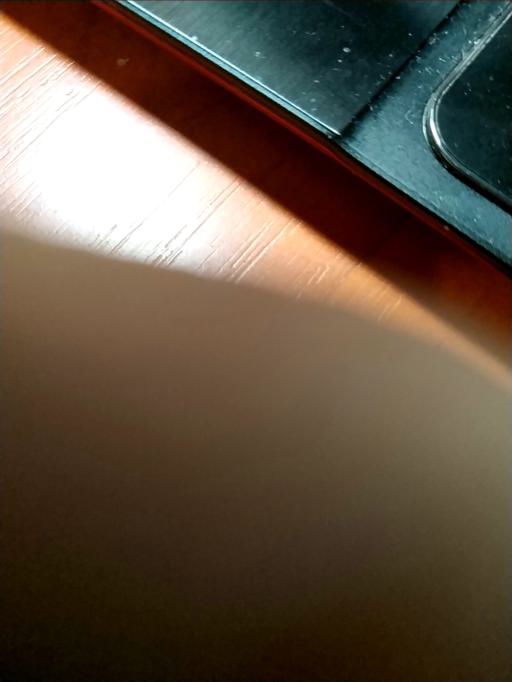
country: RU
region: Rjazan
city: Skopin
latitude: 53.9516
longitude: 39.5087
